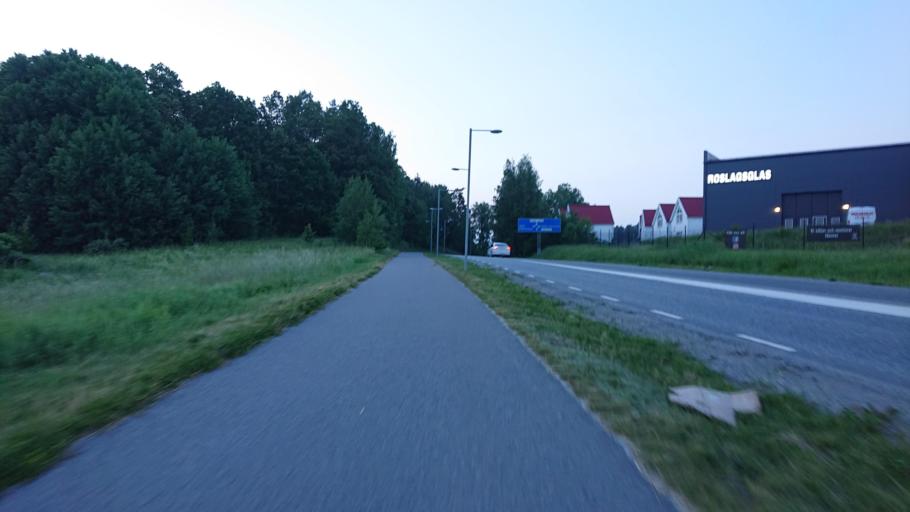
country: SE
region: Stockholm
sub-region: Osterakers Kommun
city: Akersberga
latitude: 59.4846
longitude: 18.2729
